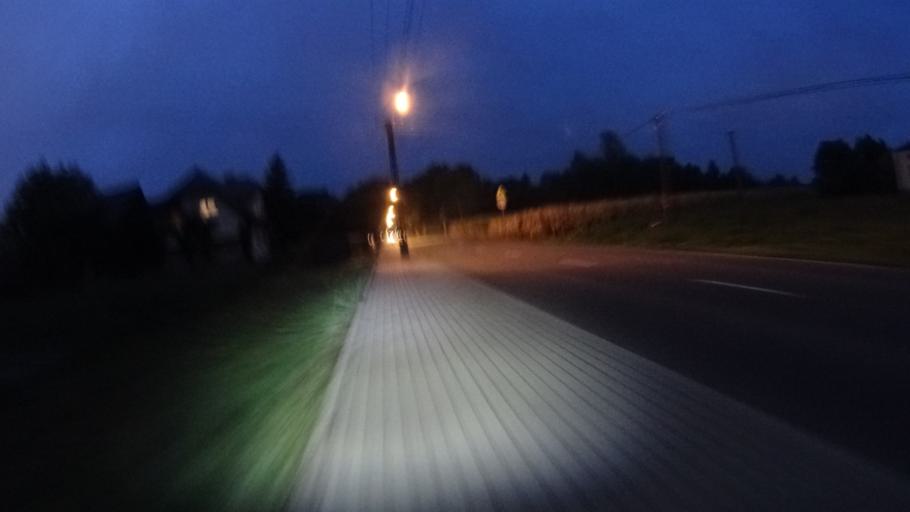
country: PL
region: Masovian Voivodeship
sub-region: Powiat warszawski zachodni
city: Babice
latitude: 52.2270
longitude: 20.8503
